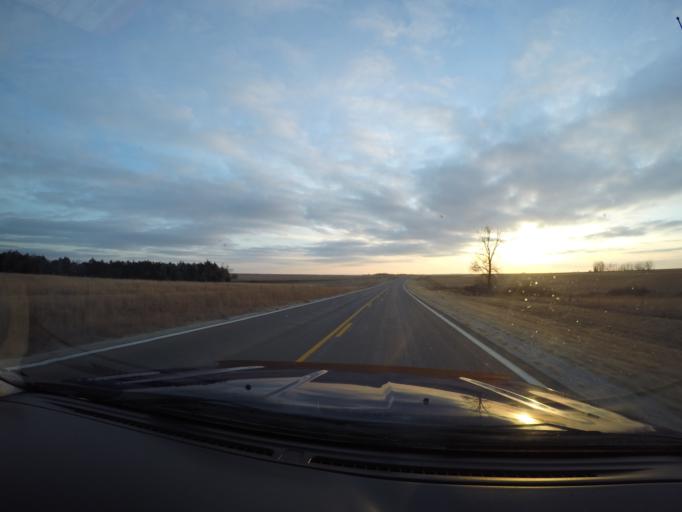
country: US
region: Kansas
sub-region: Morris County
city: Council Grove
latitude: 38.5302
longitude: -96.5254
